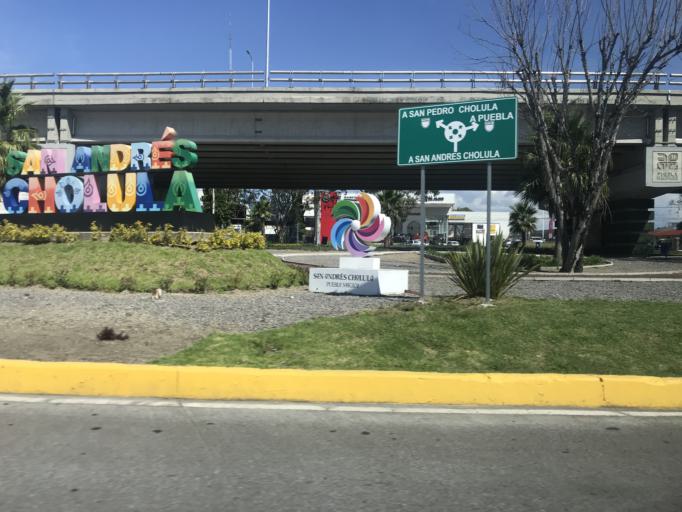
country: MX
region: Puebla
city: Cholula
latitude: 19.0597
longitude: -98.2950
